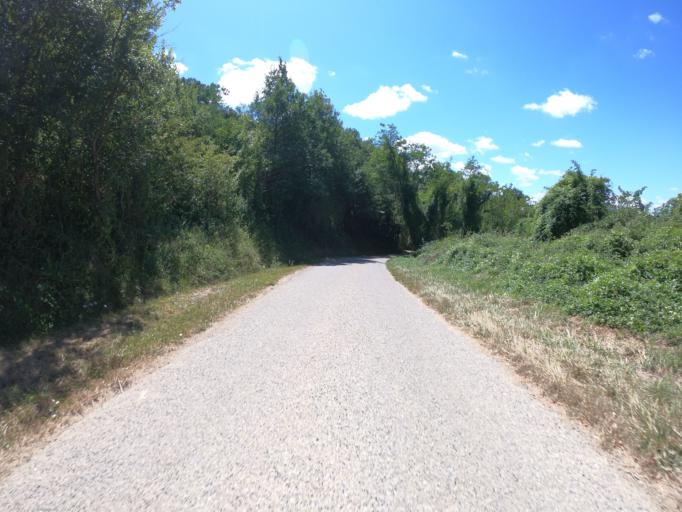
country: FR
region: Midi-Pyrenees
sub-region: Departement de l'Ariege
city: Verniolle
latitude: 43.0785
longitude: 1.7228
